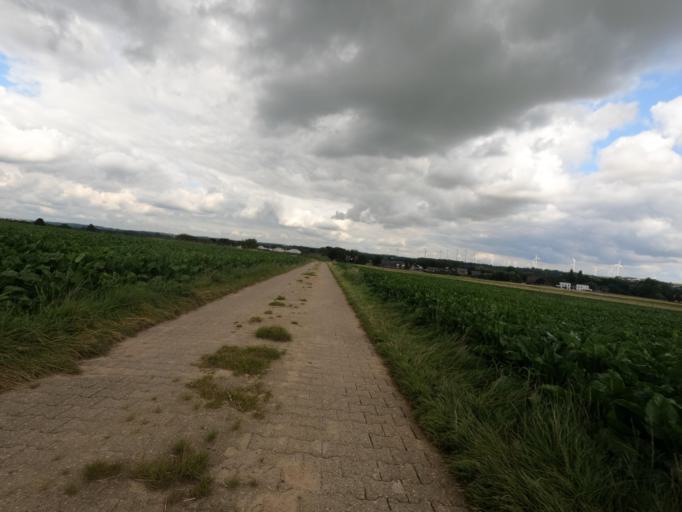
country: DE
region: North Rhine-Westphalia
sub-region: Regierungsbezirk Koln
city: Linnich
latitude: 50.9969
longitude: 6.2451
